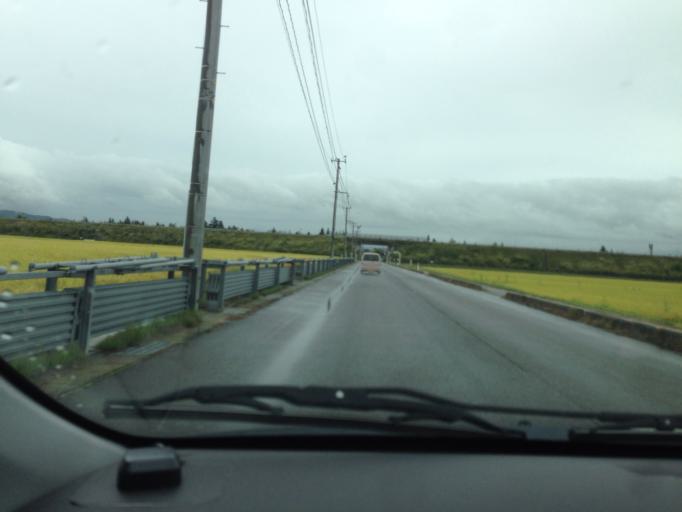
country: JP
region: Fukushima
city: Kitakata
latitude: 37.5295
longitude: 139.8209
